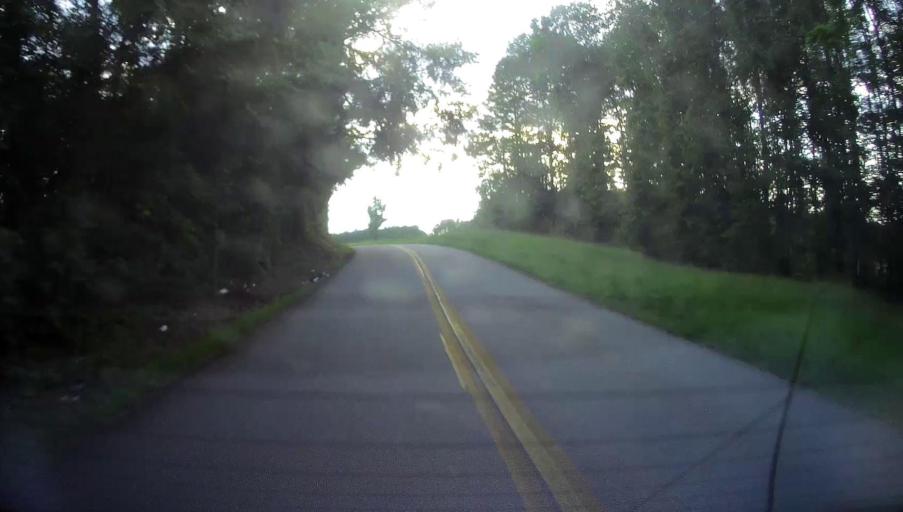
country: US
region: Georgia
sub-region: Monroe County
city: Forsyth
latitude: 33.0624
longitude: -83.9741
